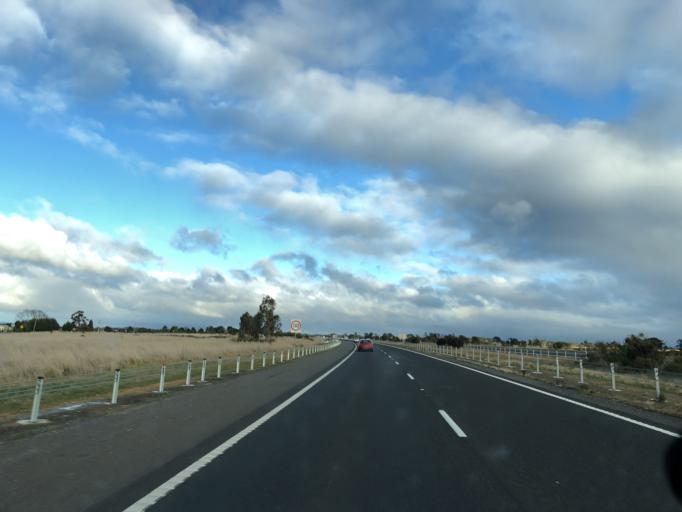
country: AU
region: Victoria
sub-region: Mount Alexander
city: Castlemaine
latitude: -37.2004
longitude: 144.4065
